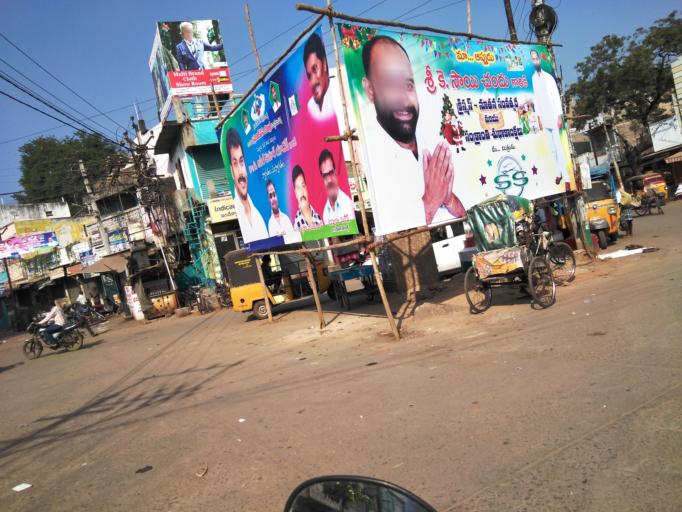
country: IN
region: Andhra Pradesh
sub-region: Nellore
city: Nellore
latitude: 14.4564
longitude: 79.9802
